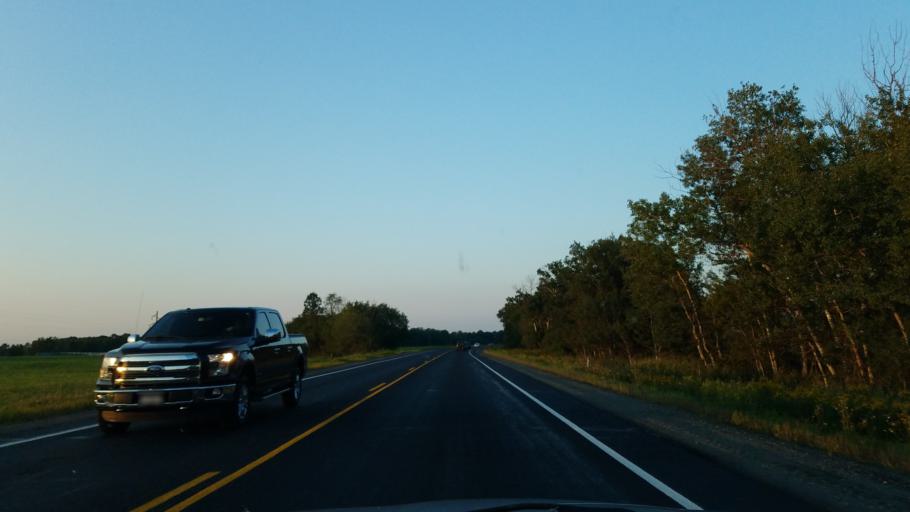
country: US
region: Wisconsin
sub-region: Polk County
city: Clear Lake
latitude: 45.3055
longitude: -92.2202
